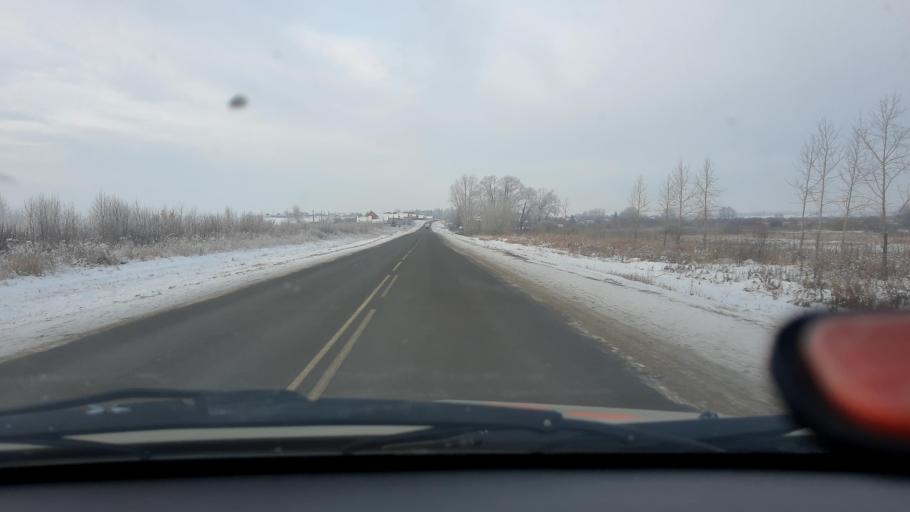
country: RU
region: Bashkortostan
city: Avdon
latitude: 54.3683
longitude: 55.8221
